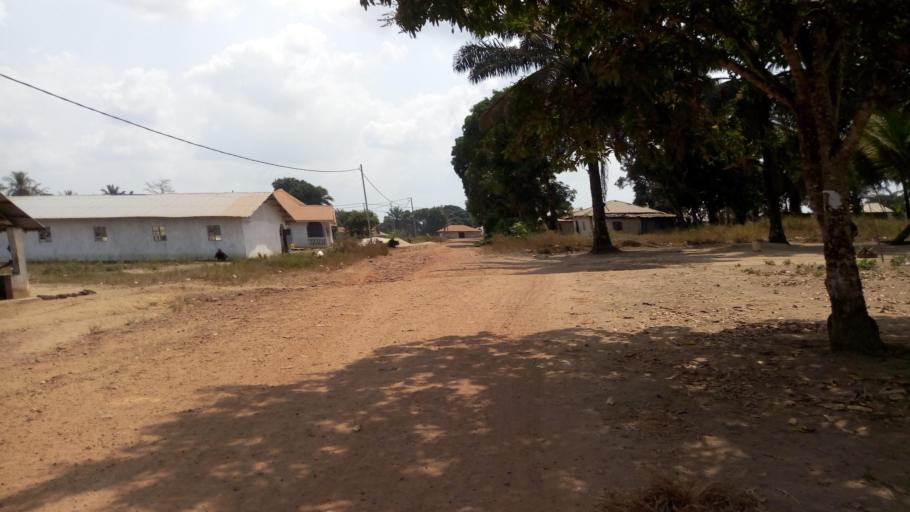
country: SL
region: Southern Province
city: Mogbwemo
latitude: 7.7911
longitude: -12.3018
